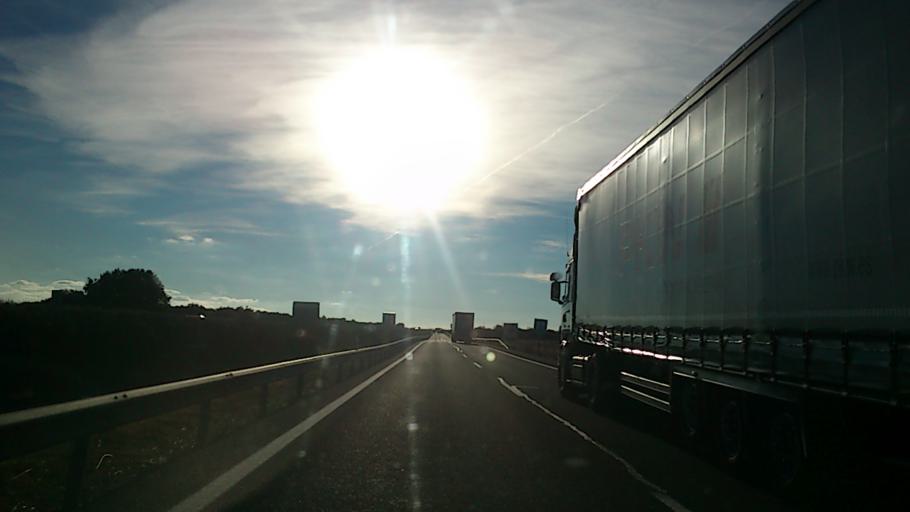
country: ES
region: Castille-La Mancha
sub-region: Provincia de Guadalajara
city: Mirabueno
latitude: 40.9250
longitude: -2.7211
